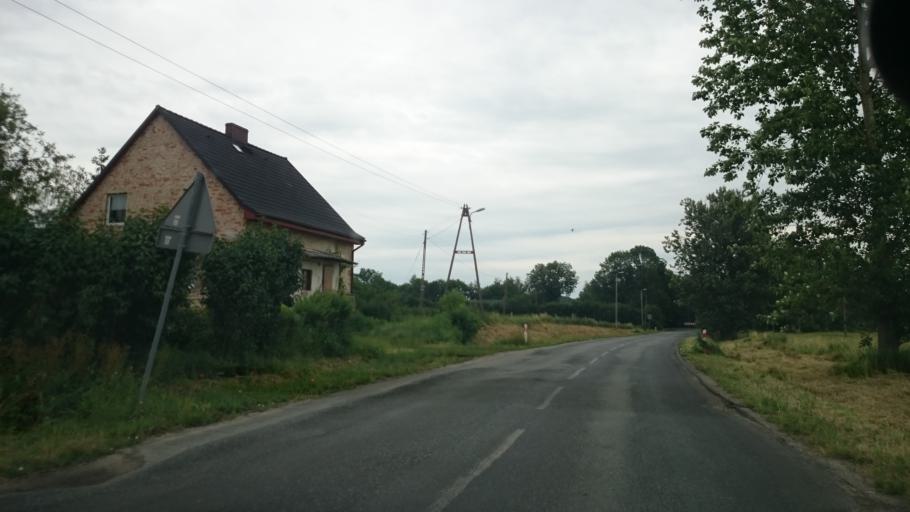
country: PL
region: Lower Silesian Voivodeship
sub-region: Powiat strzelinski
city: Przeworno
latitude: 50.6432
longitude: 17.2231
